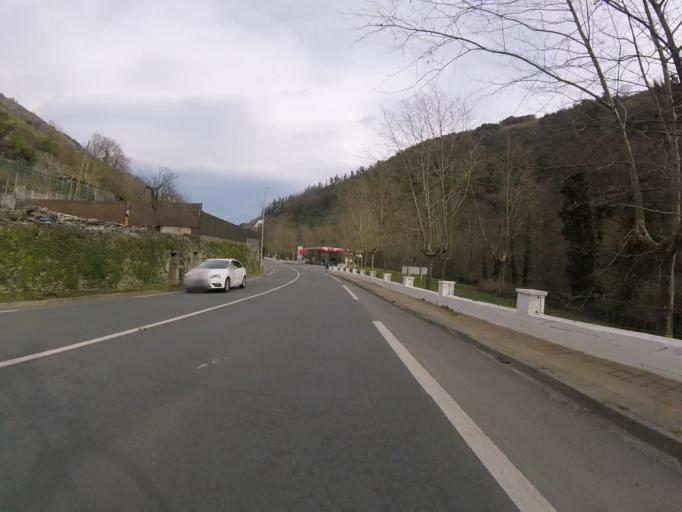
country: ES
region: Basque Country
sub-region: Provincia de Guipuzcoa
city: Azpeitia
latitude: 43.1889
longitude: -2.2596
